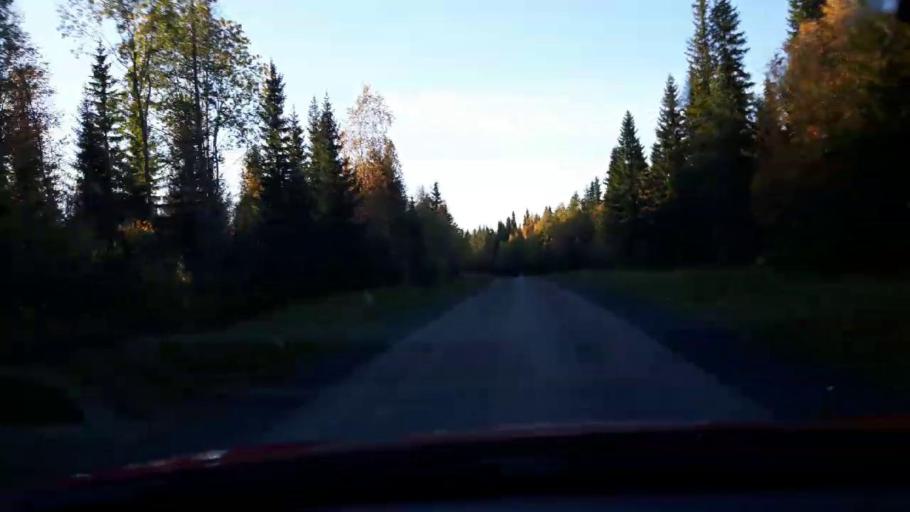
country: SE
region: Jaemtland
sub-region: Krokoms Kommun
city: Krokom
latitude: 63.4481
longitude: 14.5753
